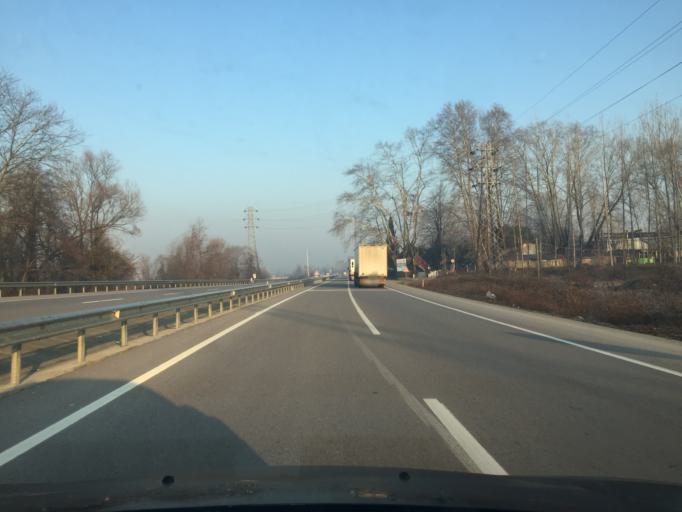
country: TR
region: Sakarya
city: Akyazi
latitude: 40.6700
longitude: 30.5888
